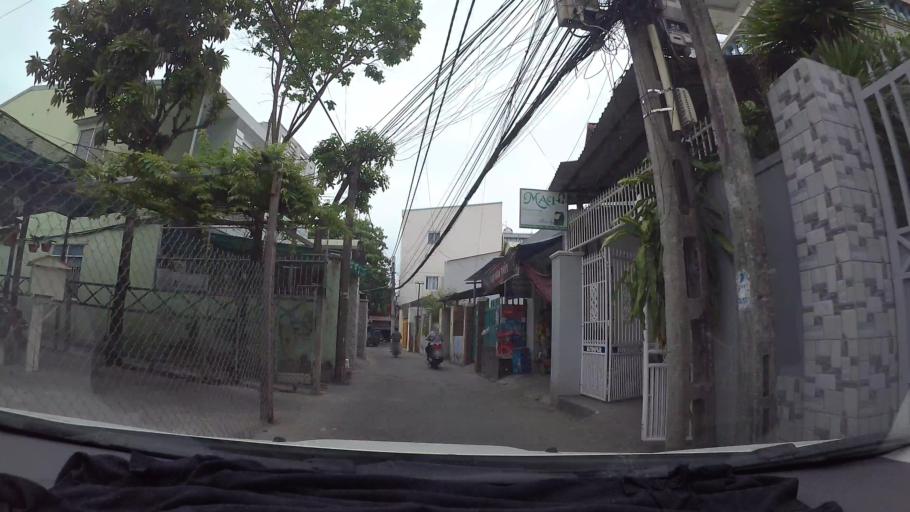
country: VN
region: Da Nang
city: Thanh Khe
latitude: 16.0628
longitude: 108.1851
